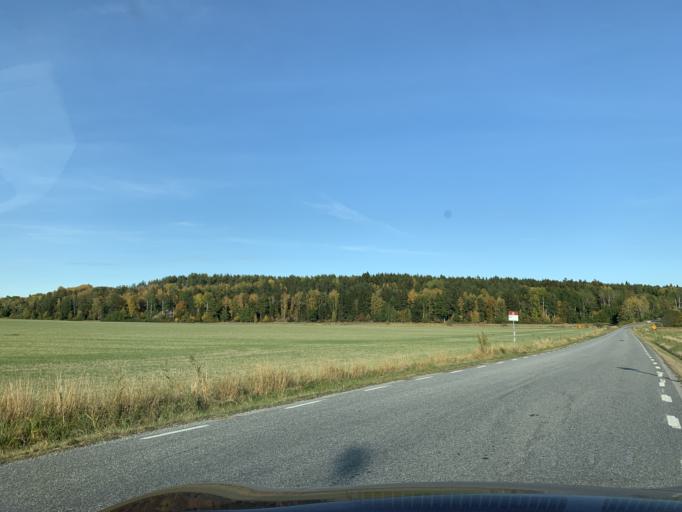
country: SE
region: Stockholm
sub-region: Upplands-Bro Kommun
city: Bro
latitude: 59.5070
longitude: 17.5846
